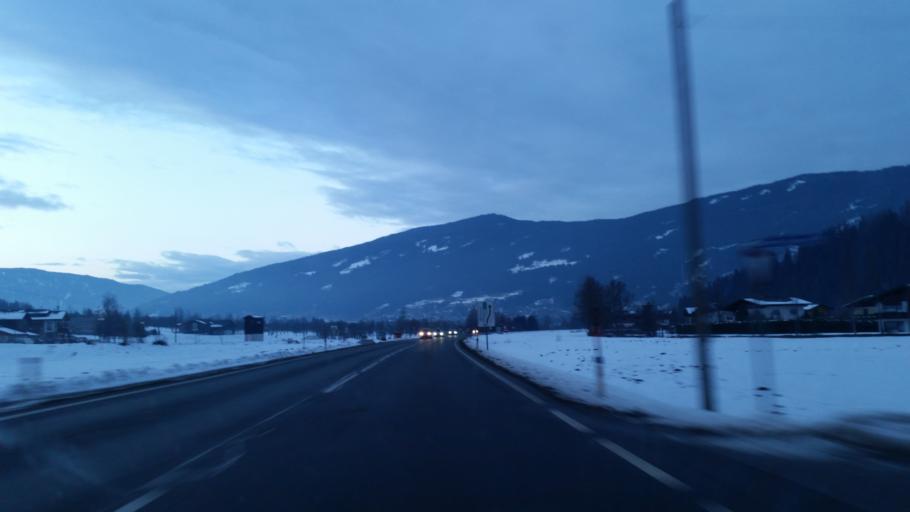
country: AT
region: Salzburg
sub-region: Politischer Bezirk Sankt Johann im Pongau
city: Radstadt
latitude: 47.3673
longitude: 13.4837
